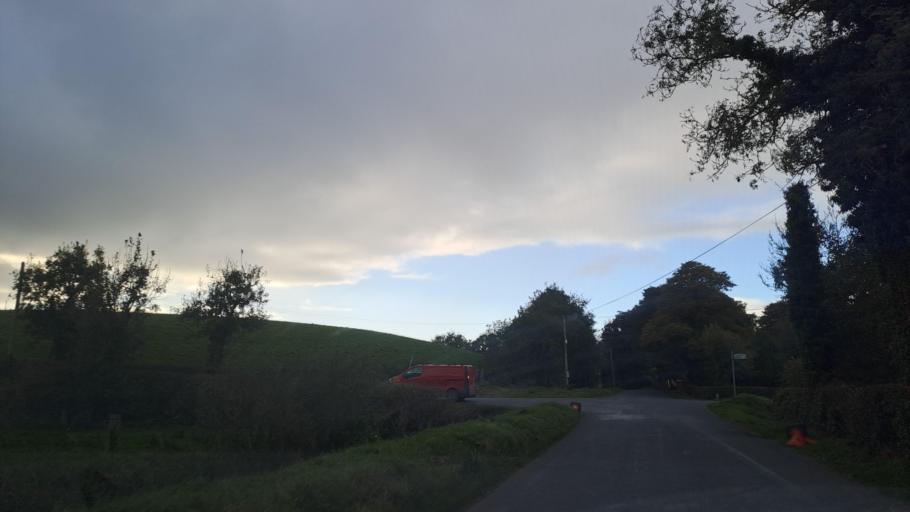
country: IE
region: Ulster
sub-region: County Monaghan
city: Castleblayney
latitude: 54.0403
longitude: -6.8292
